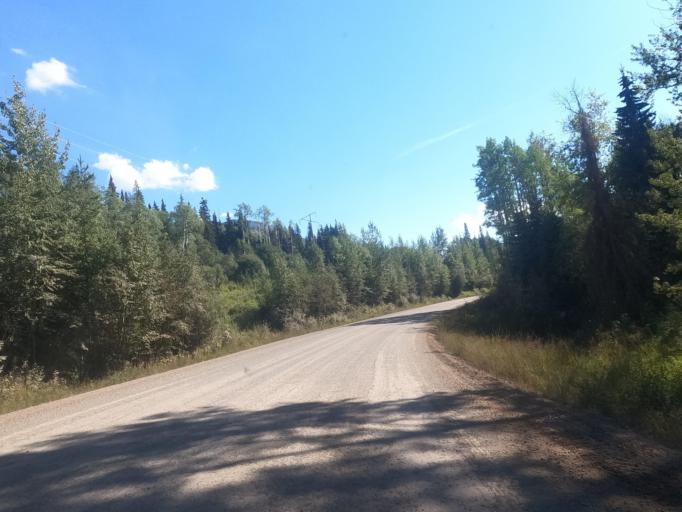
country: CA
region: British Columbia
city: Houston
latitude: 54.3004
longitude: -126.8418
